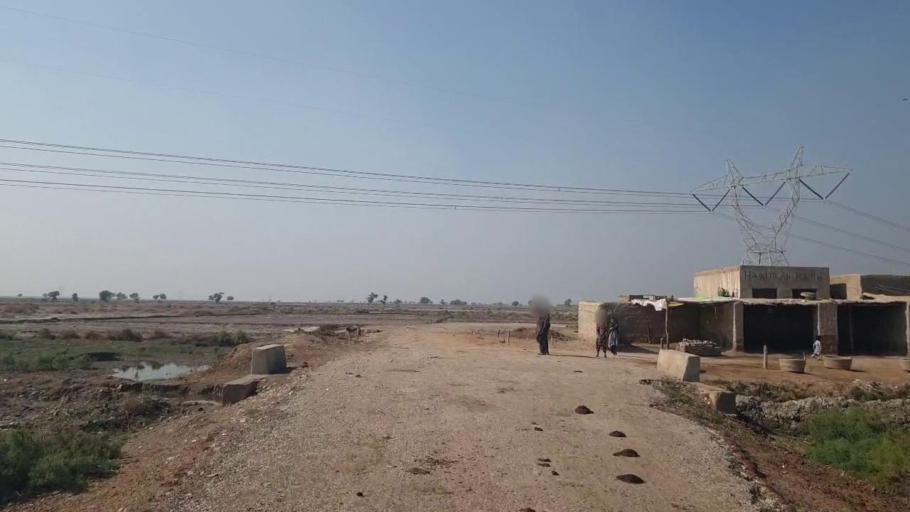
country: PK
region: Sindh
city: Sehwan
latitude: 26.4230
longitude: 67.8099
